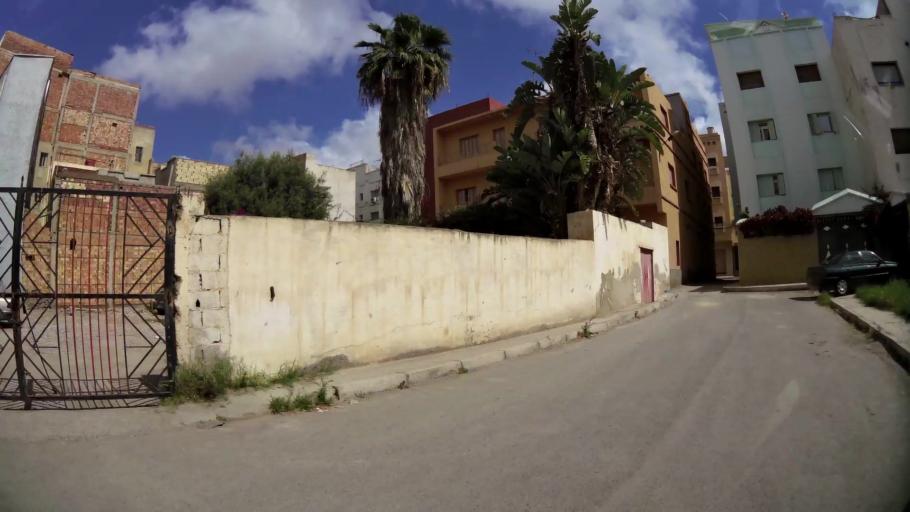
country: MA
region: Oriental
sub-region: Nador
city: Nador
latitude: 35.1626
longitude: -2.9306
